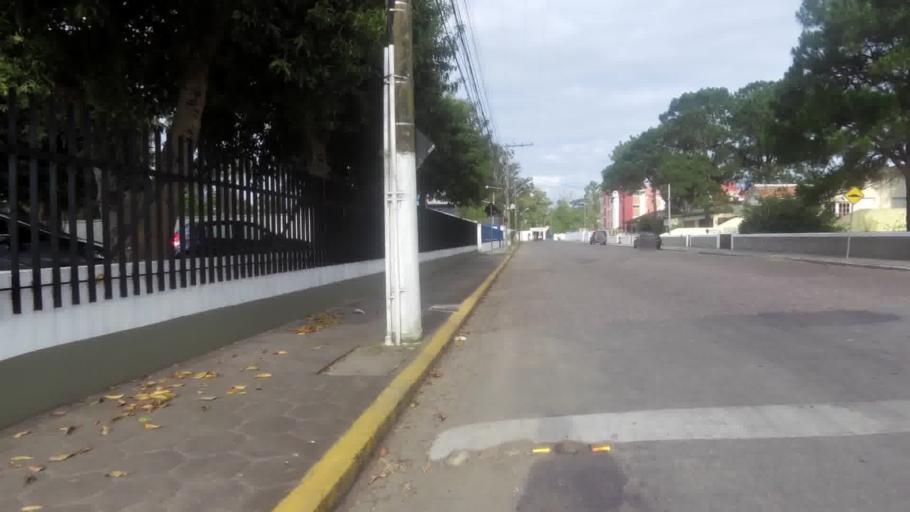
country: BR
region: Rio Grande do Sul
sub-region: Rio Grande
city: Rio Grande
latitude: -32.0311
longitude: -52.0825
